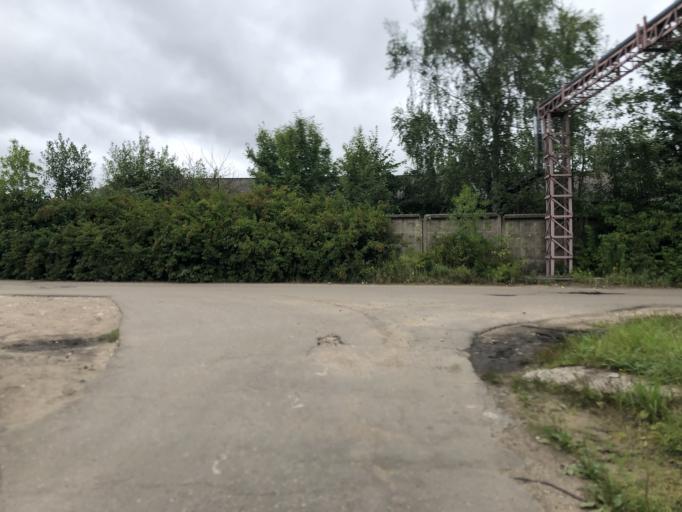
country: RU
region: Tverskaya
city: Rzhev
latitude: 56.2401
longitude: 34.3329
